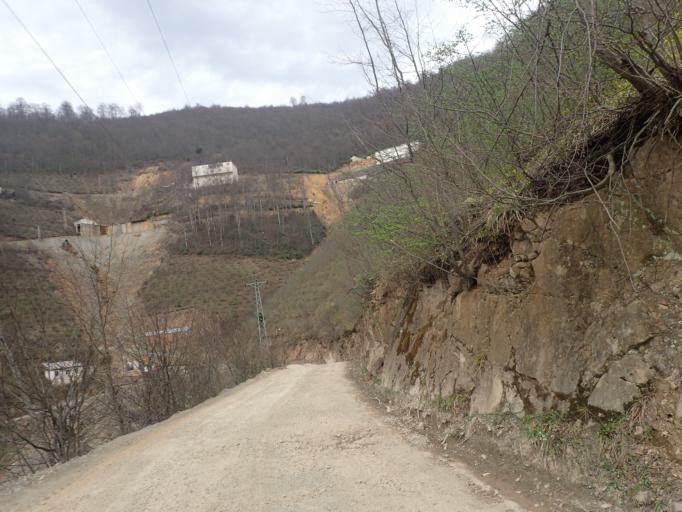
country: TR
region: Ordu
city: Kabaduz
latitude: 40.8150
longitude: 37.8860
